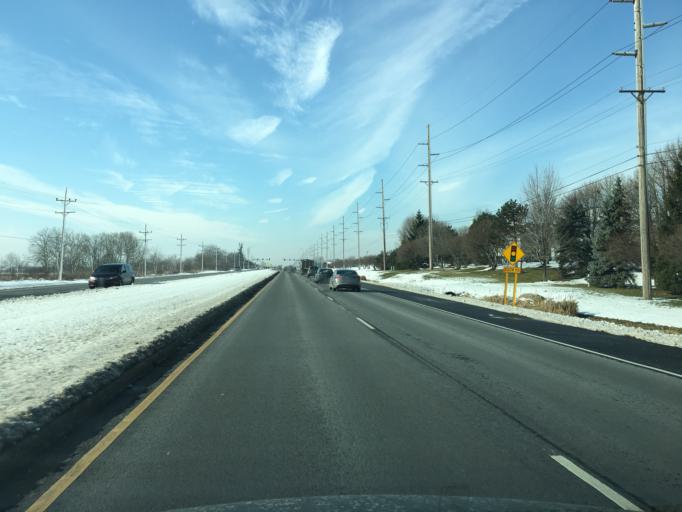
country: US
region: Illinois
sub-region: DuPage County
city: Naperville
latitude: 41.7475
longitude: -88.1814
